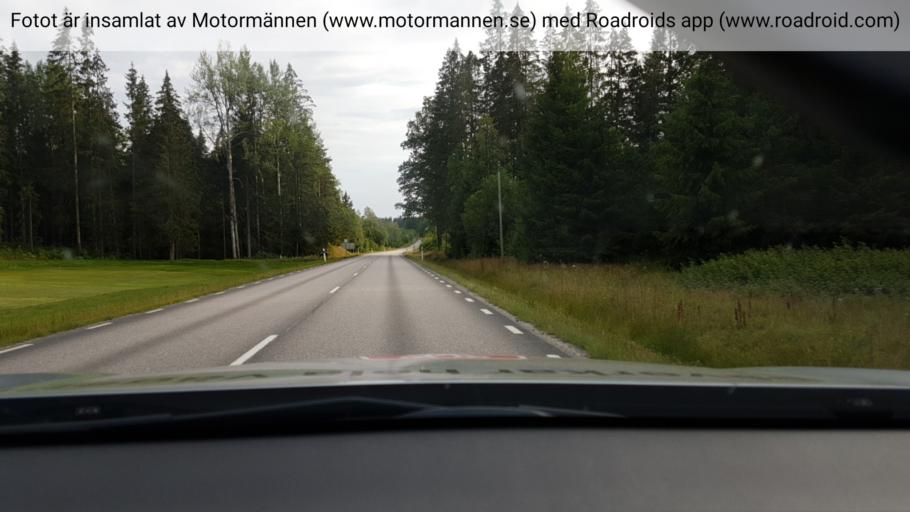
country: SE
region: Vaestra Goetaland
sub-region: Fargelanda Kommun
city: Faergelanda
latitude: 58.4489
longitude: 12.0257
